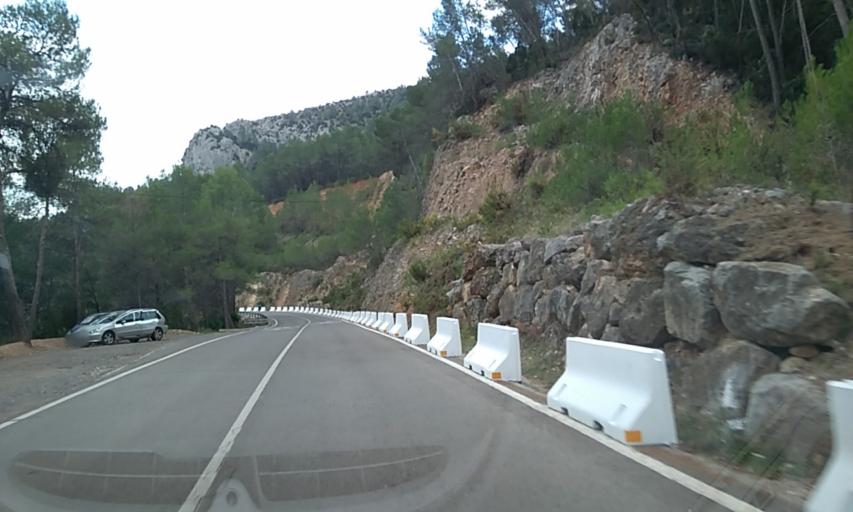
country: ES
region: Valencia
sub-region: Provincia de Castello
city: Montanejos
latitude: 40.0753
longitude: -0.5386
